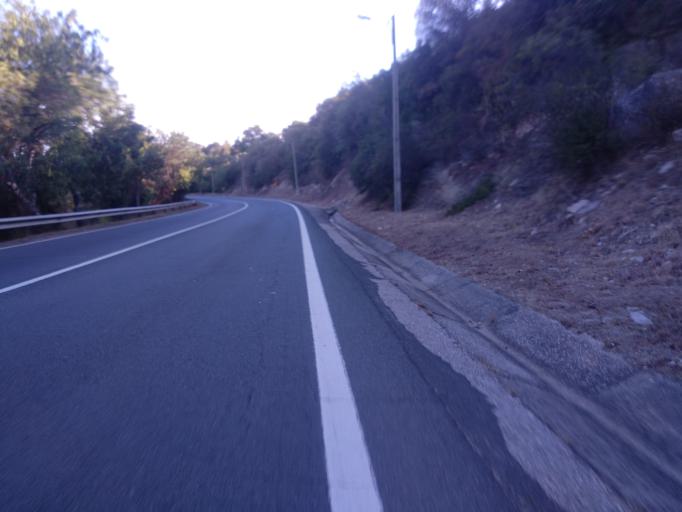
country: PT
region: Faro
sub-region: Sao Bras de Alportel
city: Sao Bras de Alportel
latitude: 37.1059
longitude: -7.9068
